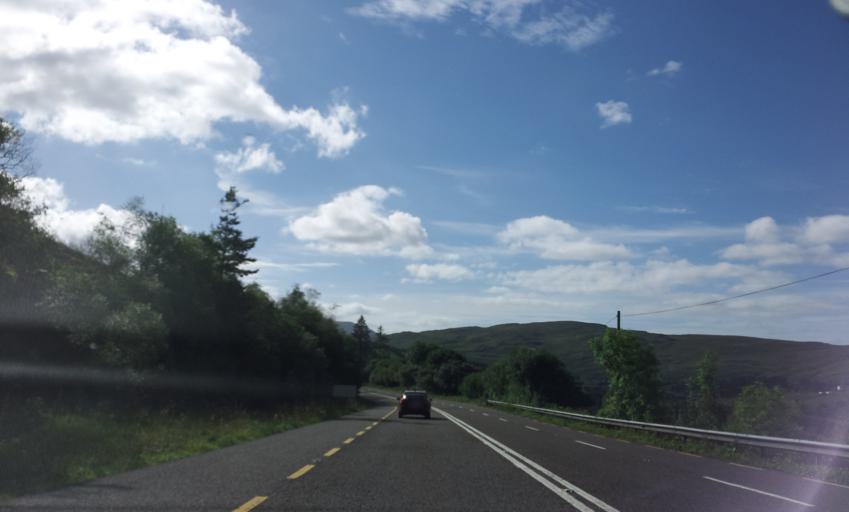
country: IE
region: Munster
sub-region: County Cork
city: Millstreet
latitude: 51.9819
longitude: -9.2678
